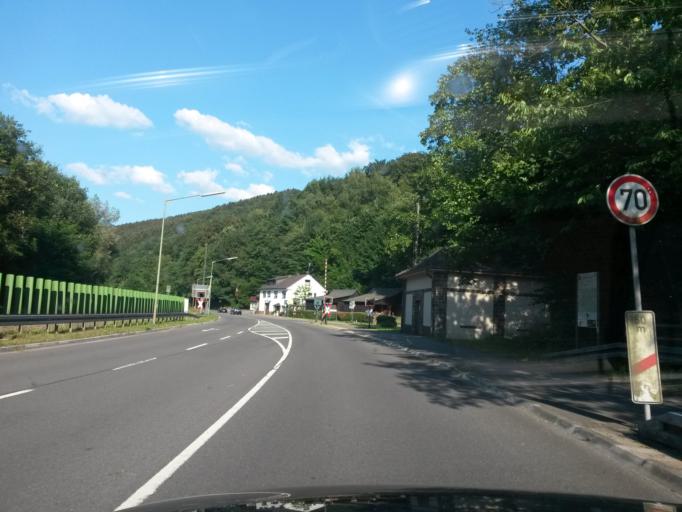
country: DE
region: North Rhine-Westphalia
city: Wiehl
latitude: 50.9860
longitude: 7.4810
